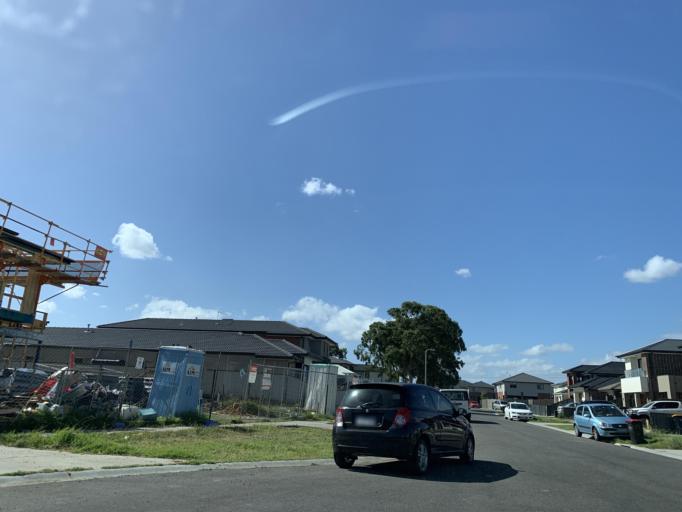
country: AU
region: Victoria
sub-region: Greater Dandenong
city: Keysborough
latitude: -38.0045
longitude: 145.1817
